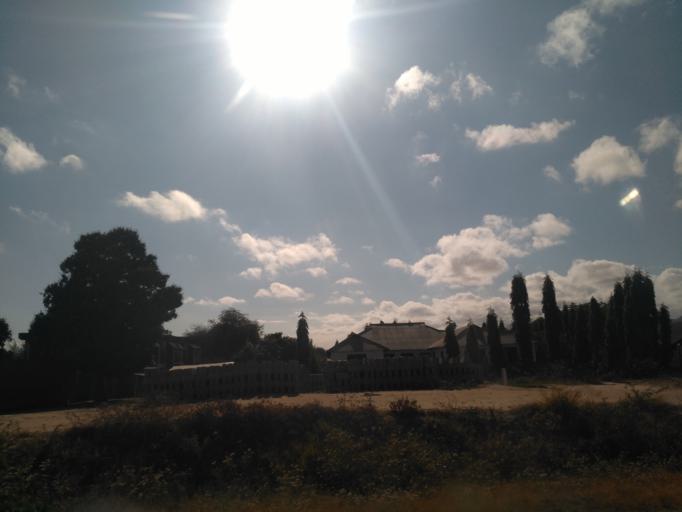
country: TZ
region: Dodoma
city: Dodoma
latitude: -6.1845
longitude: 35.7324
